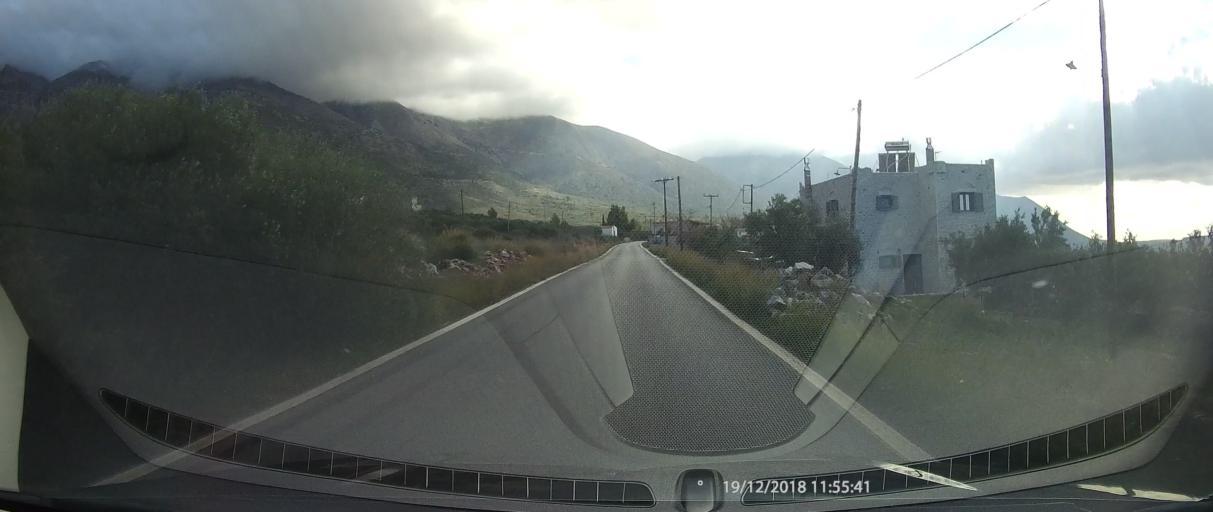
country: GR
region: Peloponnese
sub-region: Nomos Lakonias
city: Gytheio
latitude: 36.6064
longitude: 22.3954
